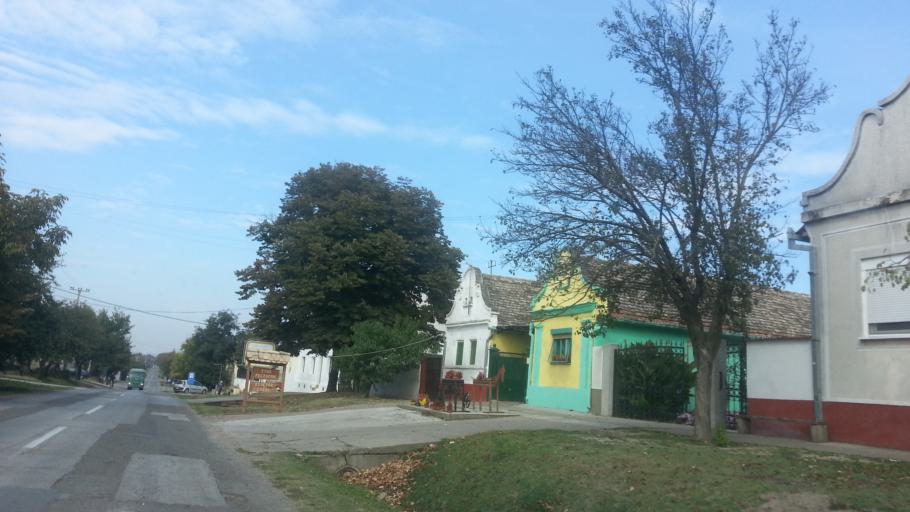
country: RS
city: Surduk
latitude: 45.0700
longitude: 20.3269
